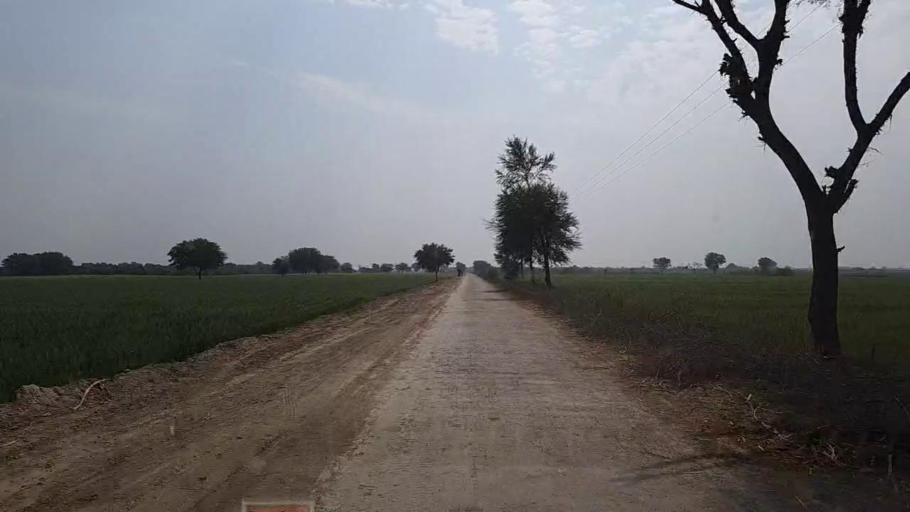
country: PK
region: Sindh
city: Mirwah Gorchani
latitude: 25.3467
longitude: 69.0536
